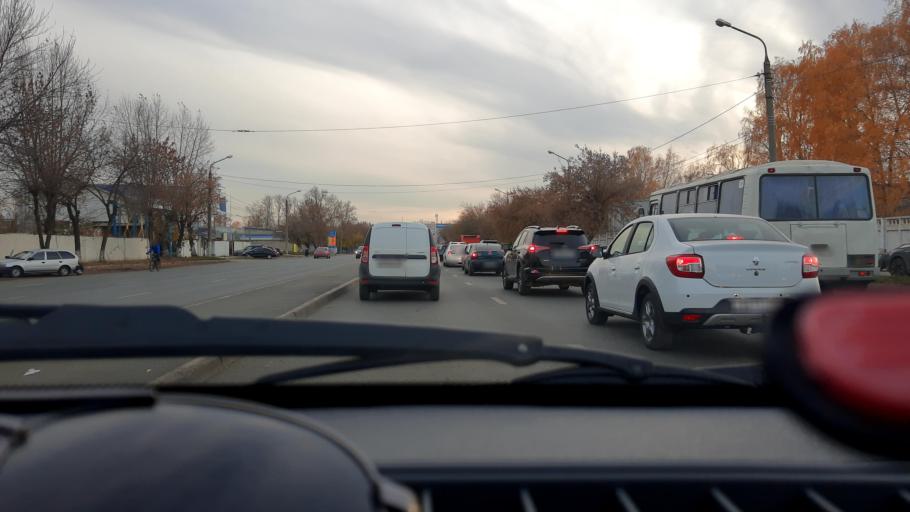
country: RU
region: Bashkortostan
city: Ufa
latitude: 54.8016
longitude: 56.0797
